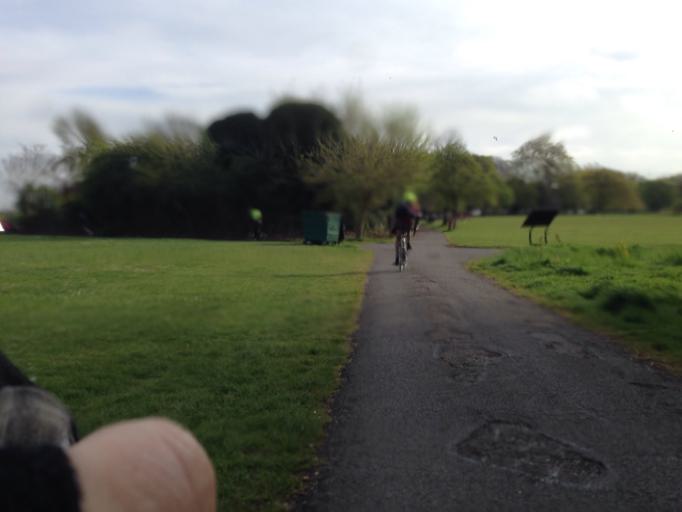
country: GB
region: England
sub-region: Greater London
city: Battersea
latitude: 51.4556
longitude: -0.1481
